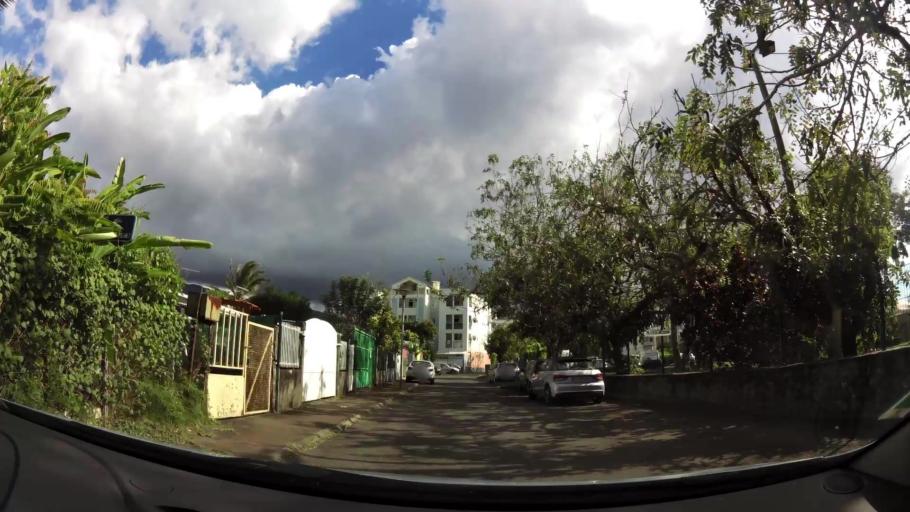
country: RE
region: Reunion
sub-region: Reunion
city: Saint-Denis
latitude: -20.8877
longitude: 55.4844
